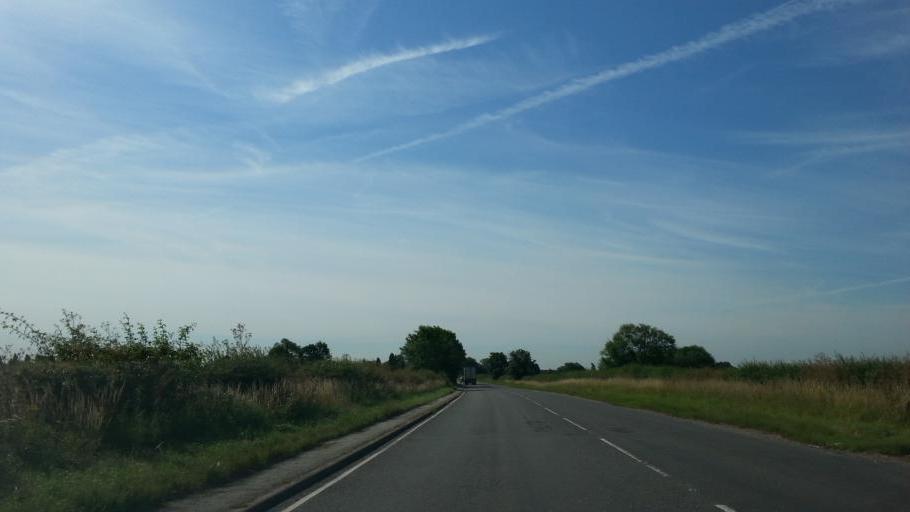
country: GB
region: England
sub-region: Nottinghamshire
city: Newark on Trent
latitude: 53.1125
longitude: -0.8204
